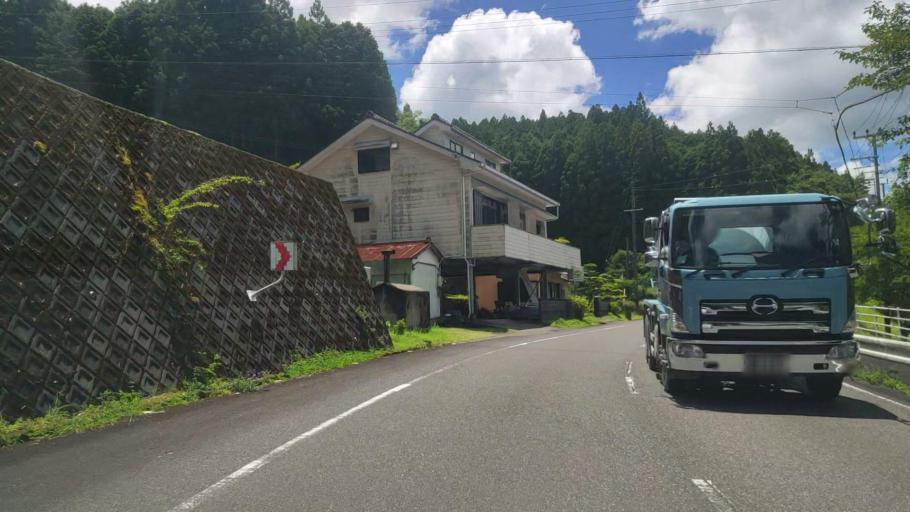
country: JP
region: Mie
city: Owase
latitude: 33.9564
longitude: 136.0702
